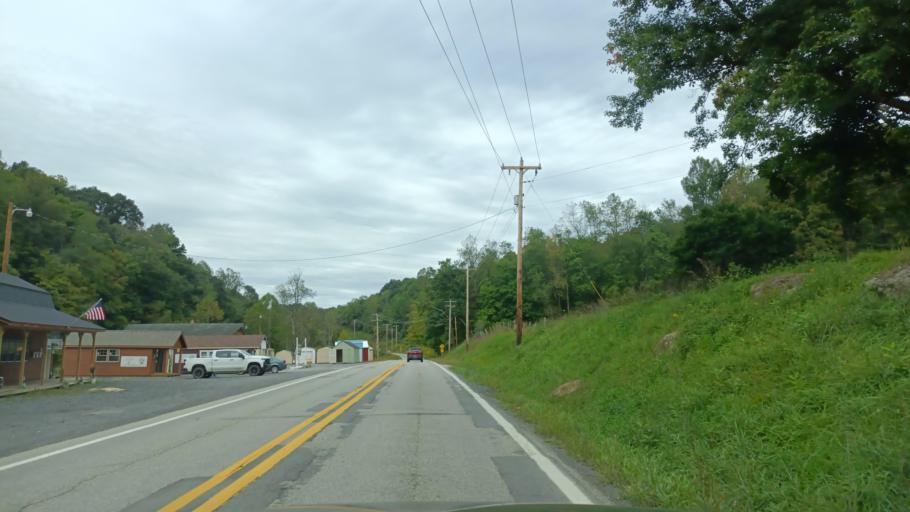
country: US
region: West Virginia
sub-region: Taylor County
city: Grafton
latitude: 39.3344
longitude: -79.8498
